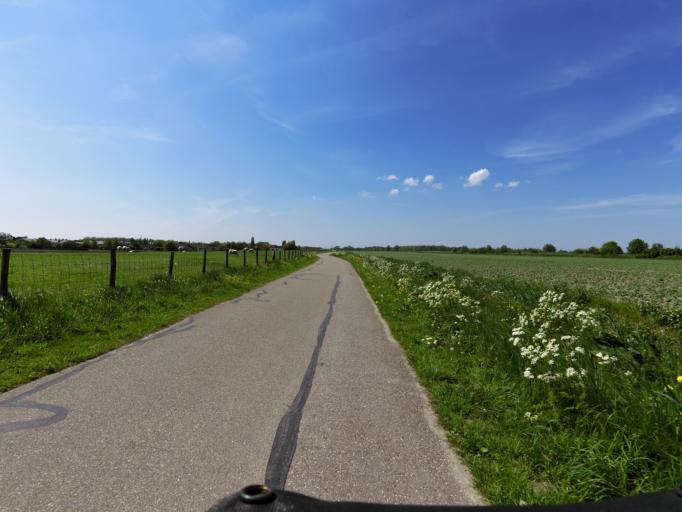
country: NL
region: South Holland
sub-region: Gemeente Binnenmaas
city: Heinenoord
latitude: 51.8284
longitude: 4.4925
